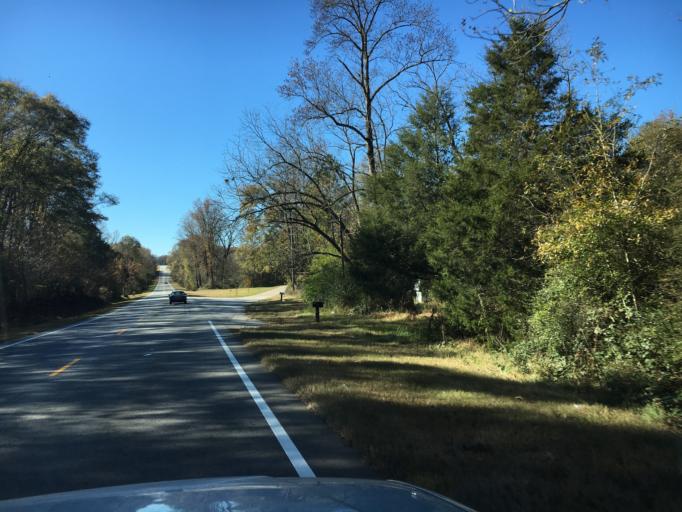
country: US
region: Georgia
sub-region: Hart County
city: Royston
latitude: 34.2944
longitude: -83.0132
